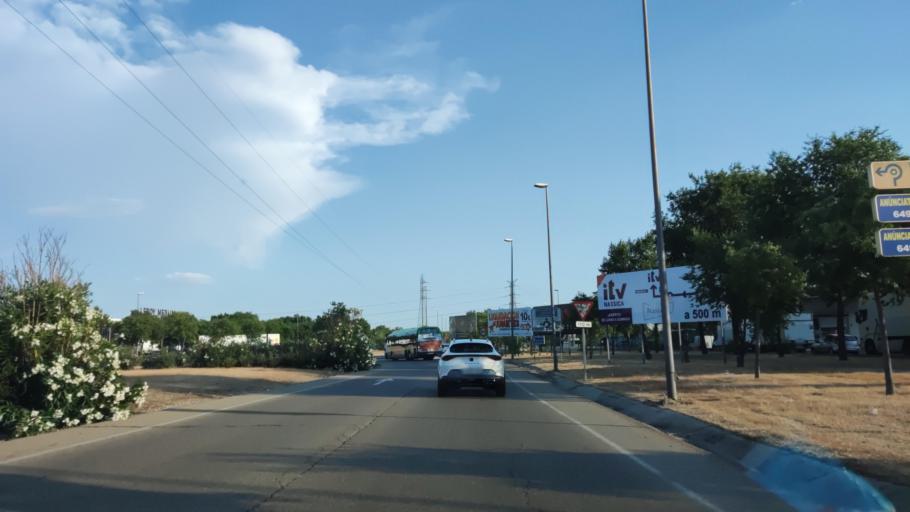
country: ES
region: Madrid
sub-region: Provincia de Madrid
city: Pinto
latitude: 40.2721
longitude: -3.7004
